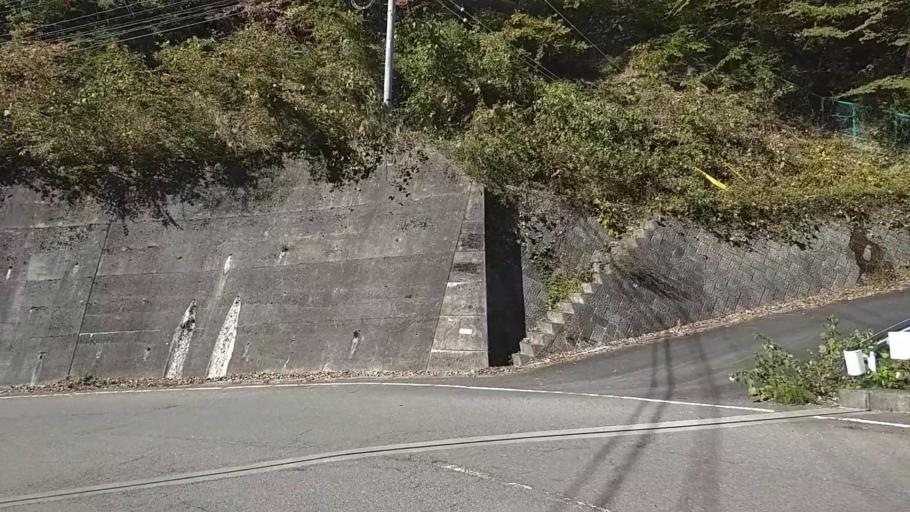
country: JP
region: Yamanashi
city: Uenohara
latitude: 35.6995
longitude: 139.0308
